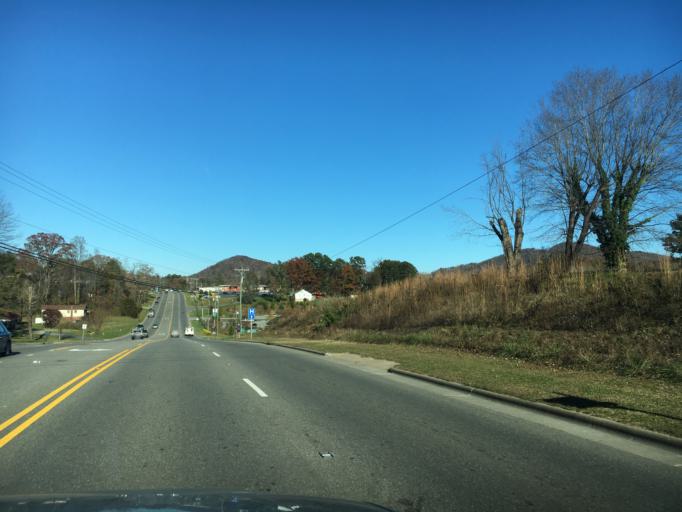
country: US
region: North Carolina
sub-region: McDowell County
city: West Marion
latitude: 35.6536
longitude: -82.0302
